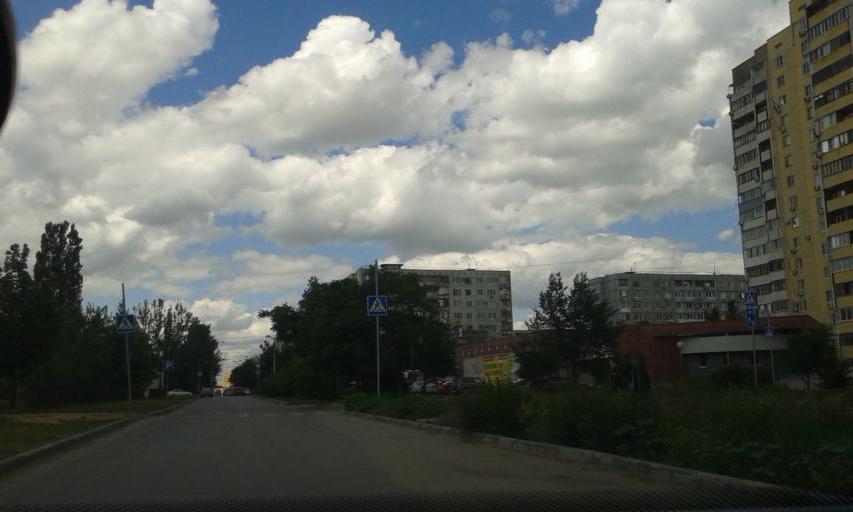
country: RU
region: Volgograd
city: Volgograd
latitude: 48.7530
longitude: 44.5046
